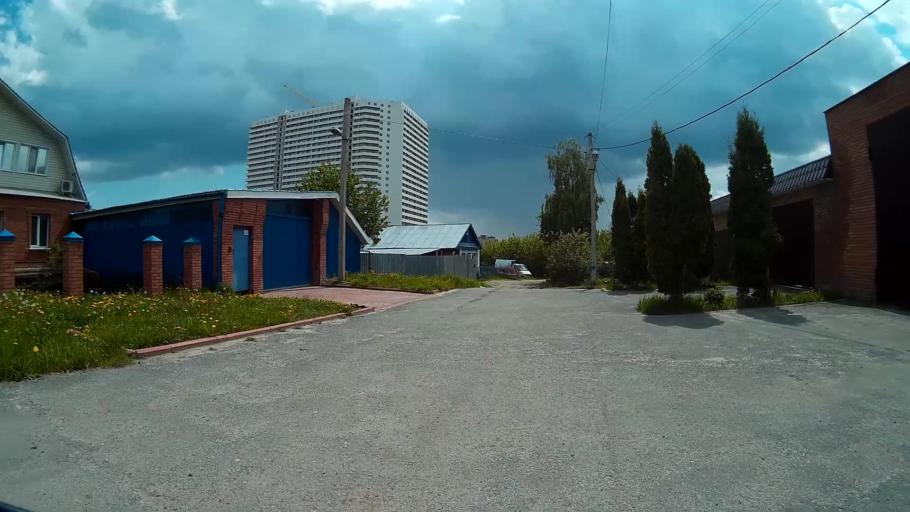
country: RU
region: Ulyanovsk
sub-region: Ulyanovskiy Rayon
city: Ulyanovsk
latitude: 54.3381
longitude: 48.3864
